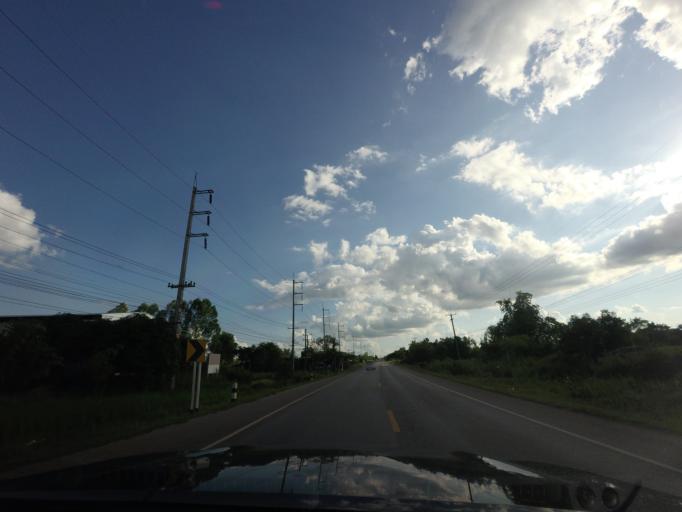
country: TH
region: Changwat Udon Thani
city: Thung Fon
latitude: 17.4997
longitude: 103.2030
